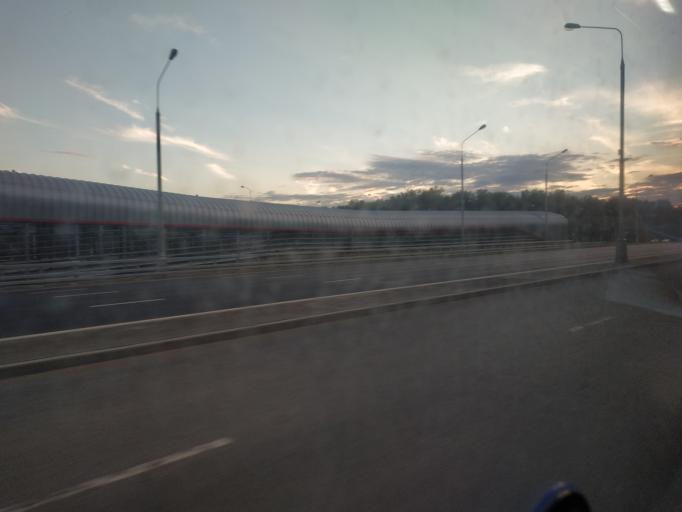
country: RU
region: Moscow
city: Solntsevo
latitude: 55.6029
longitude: 37.4060
